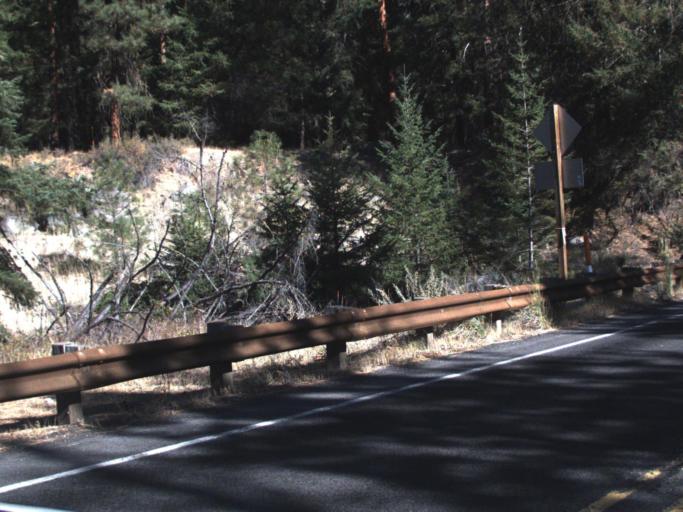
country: US
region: Washington
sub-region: Yakima County
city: Tieton
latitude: 46.6733
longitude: -121.0843
